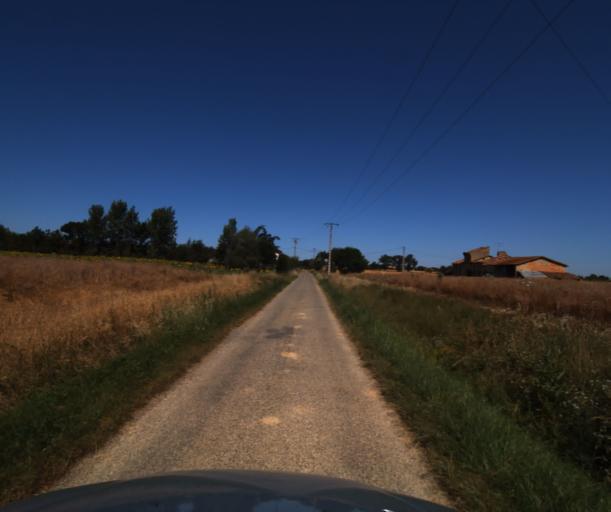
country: FR
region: Midi-Pyrenees
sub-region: Departement de la Haute-Garonne
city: Muret
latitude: 43.4534
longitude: 1.3653
